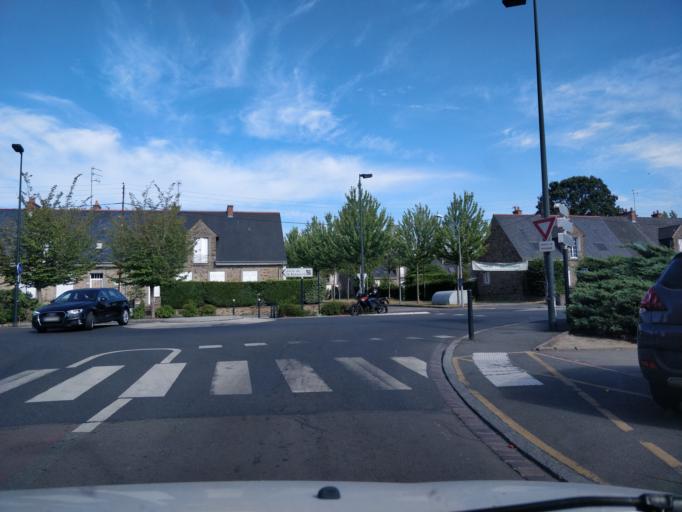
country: FR
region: Pays de la Loire
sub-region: Departement de la Loire-Atlantique
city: Nantes
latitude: 47.2452
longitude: -1.5335
